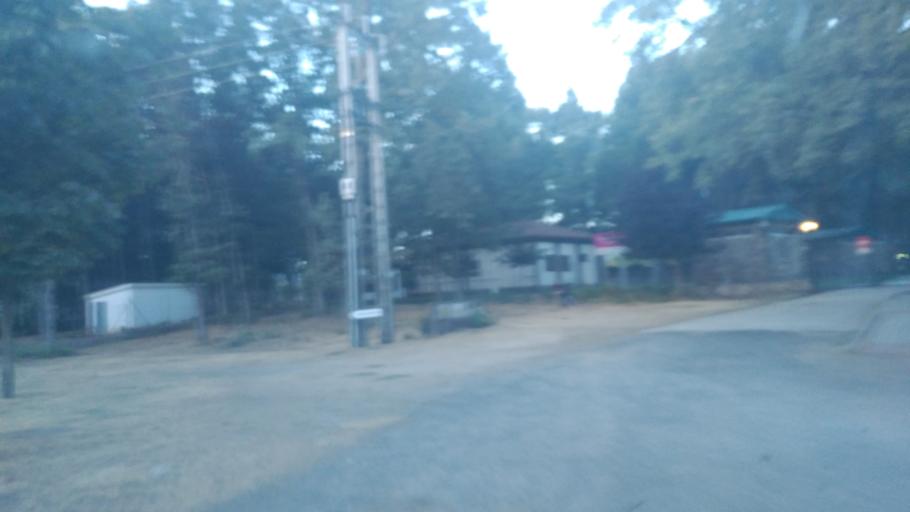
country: ES
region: Castille and Leon
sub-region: Provincia de Salamanca
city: Nava de Francia
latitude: 40.5183
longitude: -6.1002
